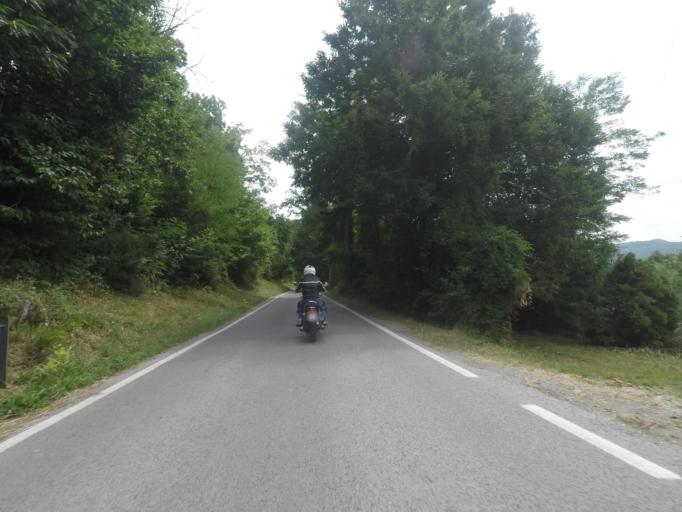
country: IT
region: Tuscany
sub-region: Provincia di Lucca
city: Castelnuovo di Garfagnana
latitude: 44.1122
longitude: 10.3885
